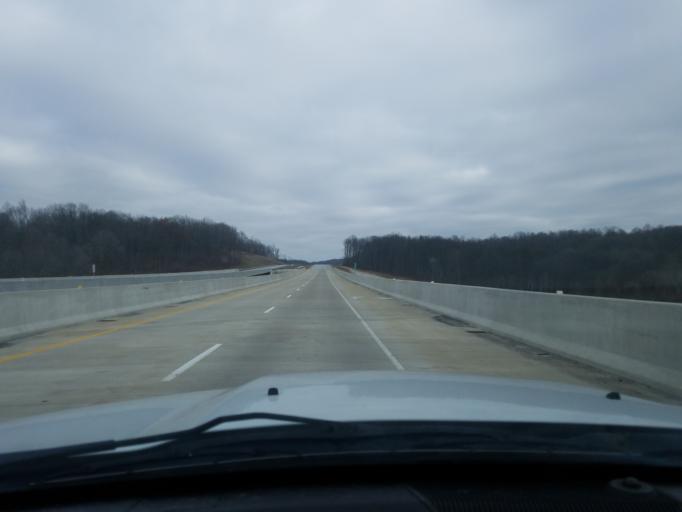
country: US
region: Indiana
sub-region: Greene County
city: Bloomfield
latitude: 38.9636
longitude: -86.7992
